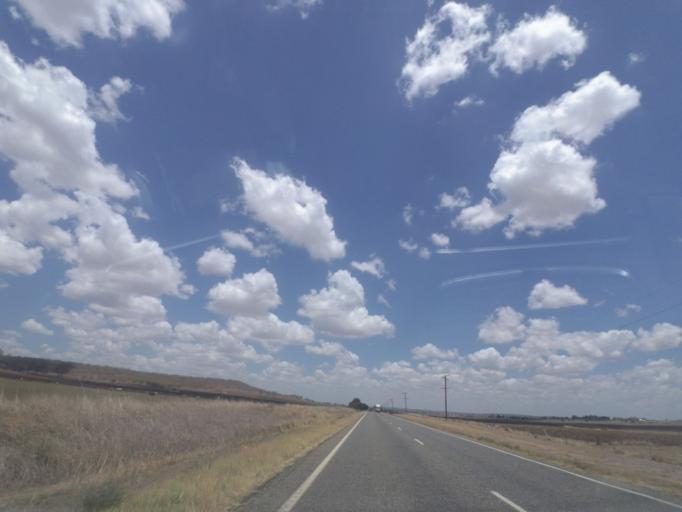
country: AU
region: Queensland
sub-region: Southern Downs
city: Warwick
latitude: -28.0046
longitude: 151.9915
